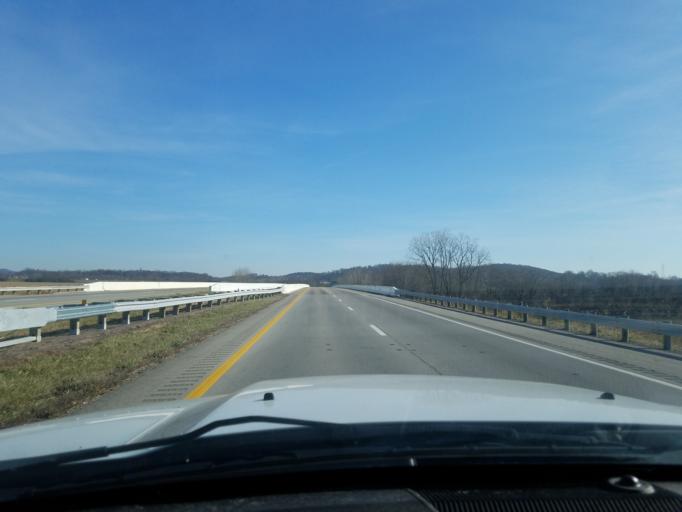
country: US
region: Ohio
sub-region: Pike County
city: Piketon
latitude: 39.0463
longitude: -83.0408
